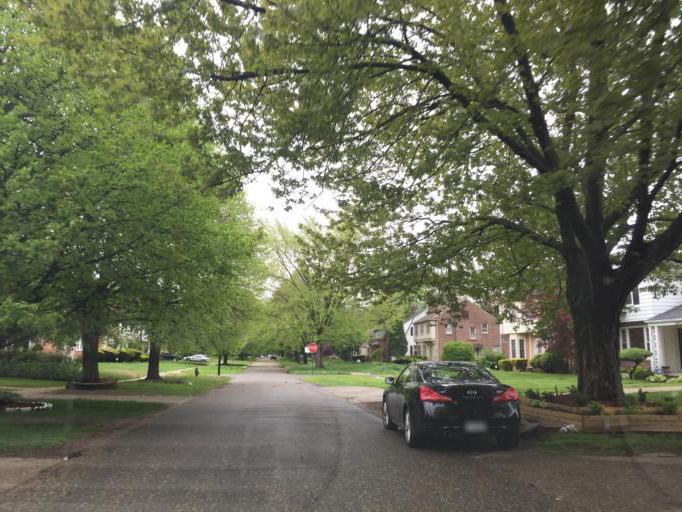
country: US
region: Michigan
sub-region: Oakland County
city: Southfield
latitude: 42.4140
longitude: -83.2343
